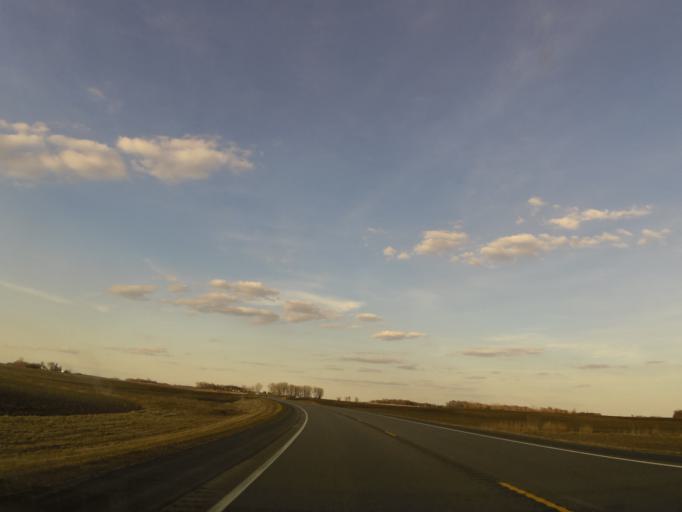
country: US
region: Minnesota
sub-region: McLeod County
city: Glencoe
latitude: 44.7334
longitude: -94.2927
